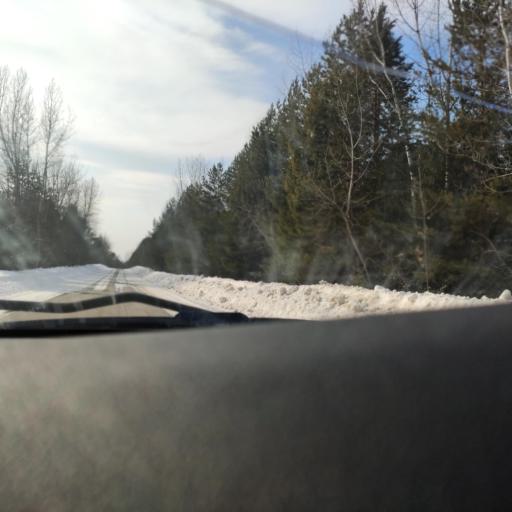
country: RU
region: Samara
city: Rozhdestveno
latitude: 53.2519
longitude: 49.9375
